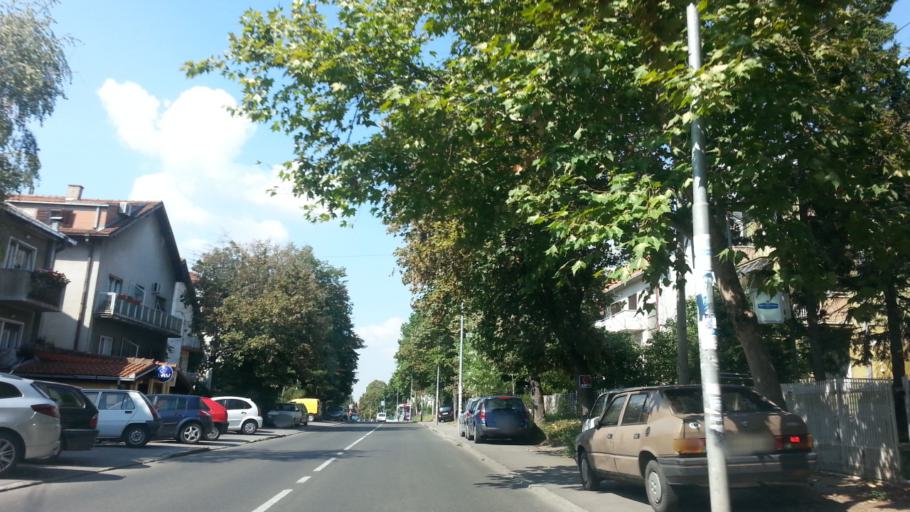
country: RS
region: Central Serbia
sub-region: Belgrade
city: Cukarica
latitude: 44.7673
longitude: 20.4219
